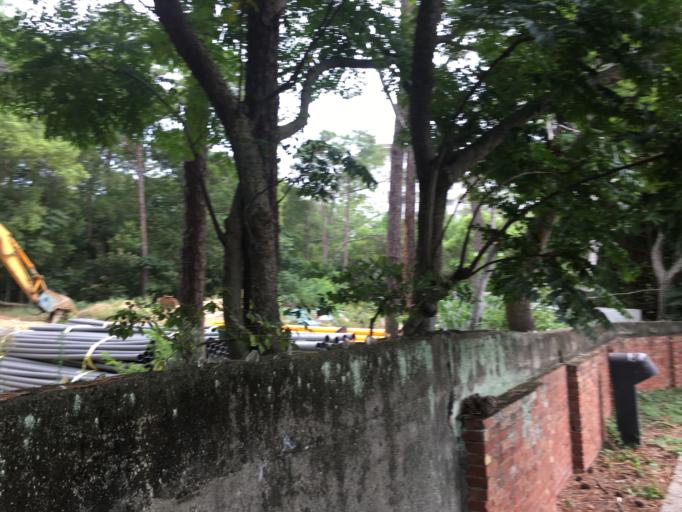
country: TW
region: Taiwan
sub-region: Hsinchu
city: Hsinchu
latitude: 24.7896
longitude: 120.9942
